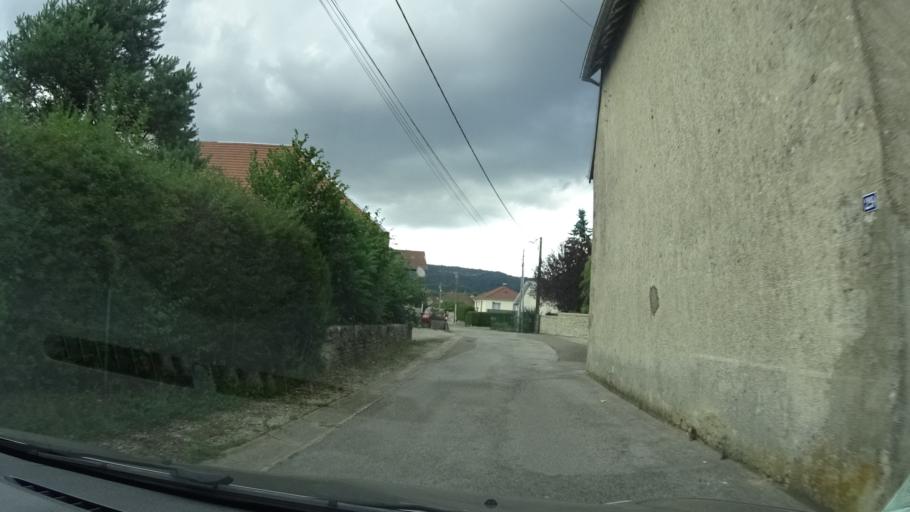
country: FR
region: Franche-Comte
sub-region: Departement du Doubs
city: Saone
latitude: 47.2180
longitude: 6.1108
